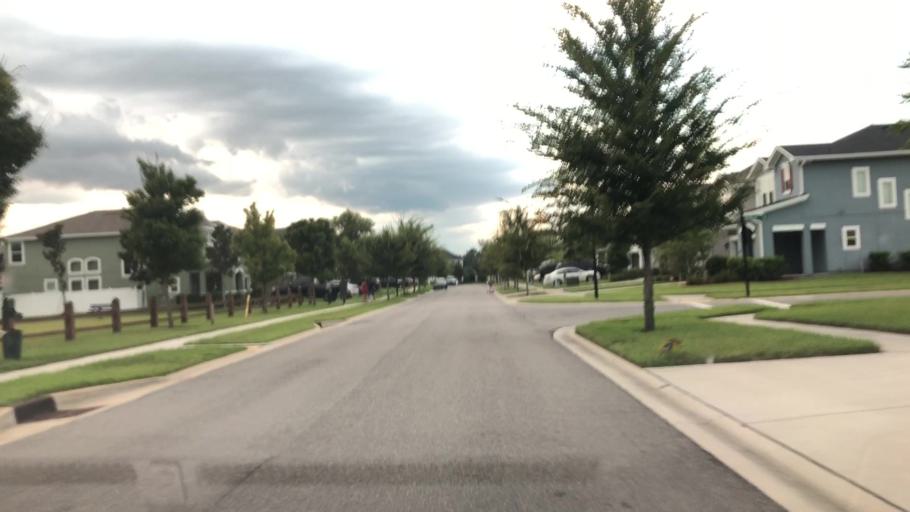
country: US
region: Florida
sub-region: Saint Johns County
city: Palm Valley
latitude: 30.0965
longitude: -81.4628
